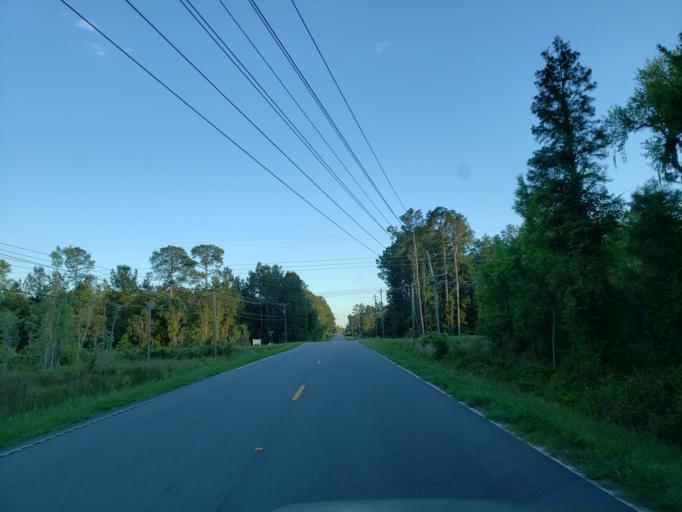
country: US
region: Georgia
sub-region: Lowndes County
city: Valdosta
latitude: 30.7117
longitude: -83.2423
